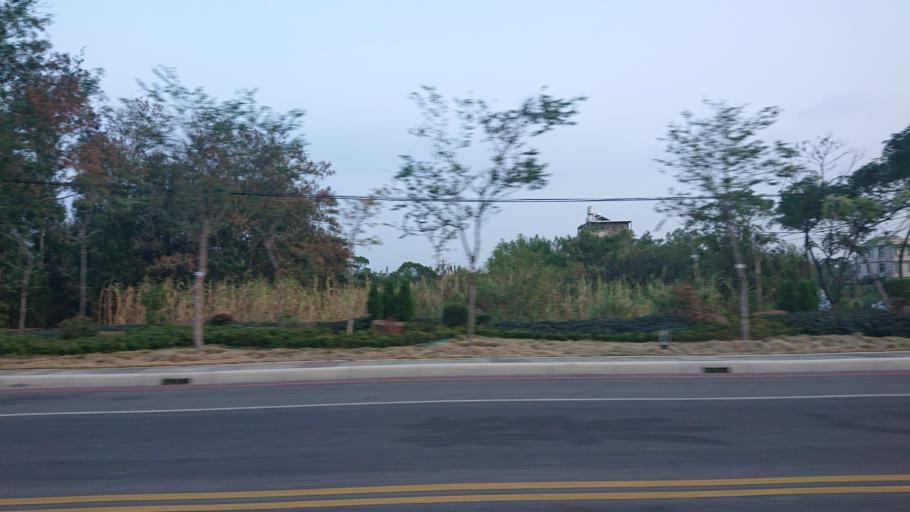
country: TW
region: Fukien
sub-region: Kinmen
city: Jincheng
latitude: 24.4443
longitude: 118.3260
